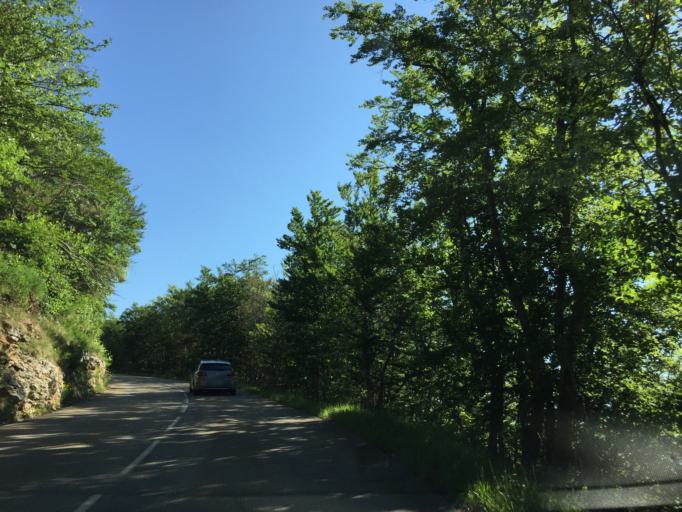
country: FR
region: Rhone-Alpes
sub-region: Departement de la Drome
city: Saint-Laurent-en-Royans
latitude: 44.9151
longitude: 5.3707
